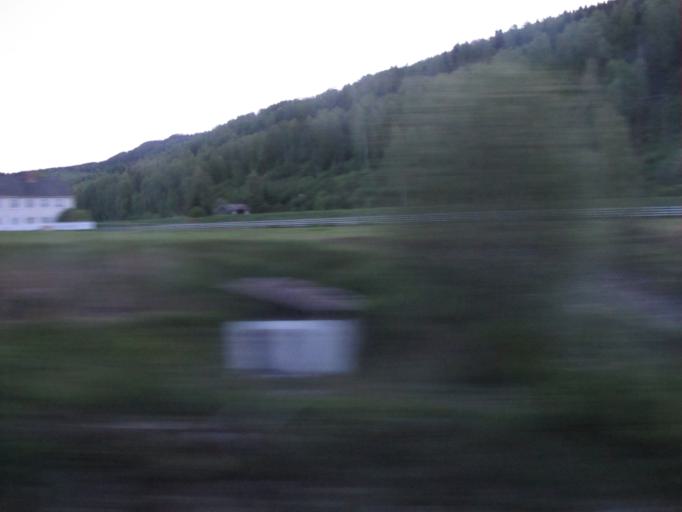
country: NO
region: Oppland
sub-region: Nord-Fron
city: Vinstra
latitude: 61.5849
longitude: 9.8070
